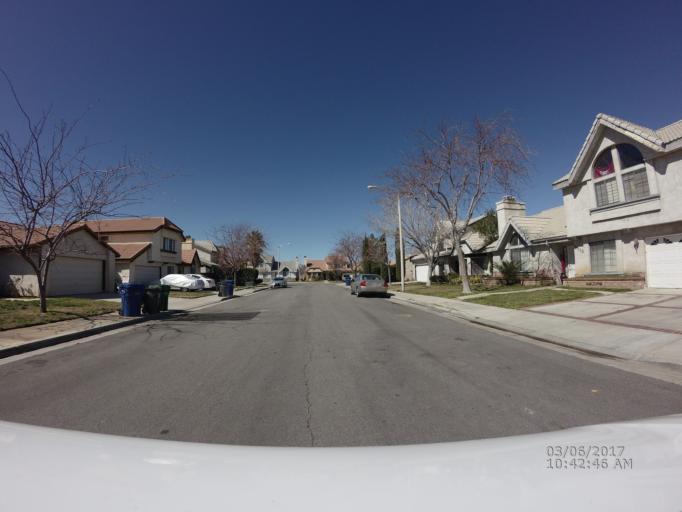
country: US
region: California
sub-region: Los Angeles County
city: Quartz Hill
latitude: 34.6536
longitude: -118.2214
